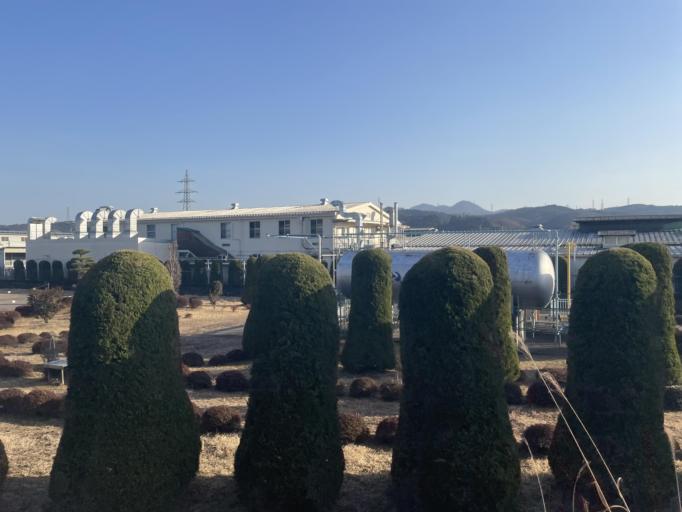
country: JP
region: Gunma
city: Nakanojomachi
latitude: 36.5848
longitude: 138.8434
